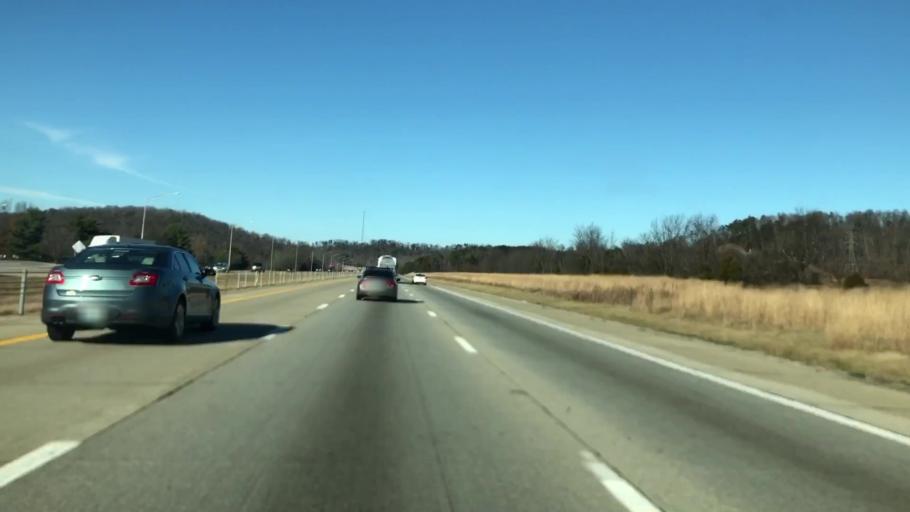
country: US
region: Kentucky
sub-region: Bullitt County
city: Shepherdsville
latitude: 37.9423
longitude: -85.6885
